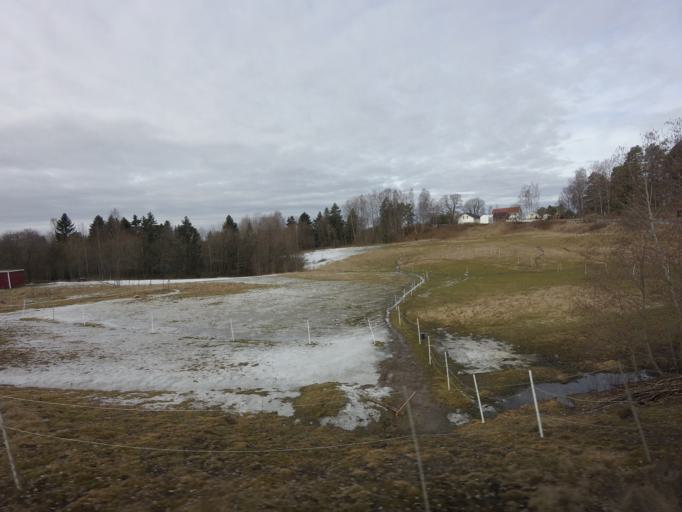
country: NO
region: Akershus
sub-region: Enebakk
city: Flateby
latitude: 59.8549
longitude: 11.2368
